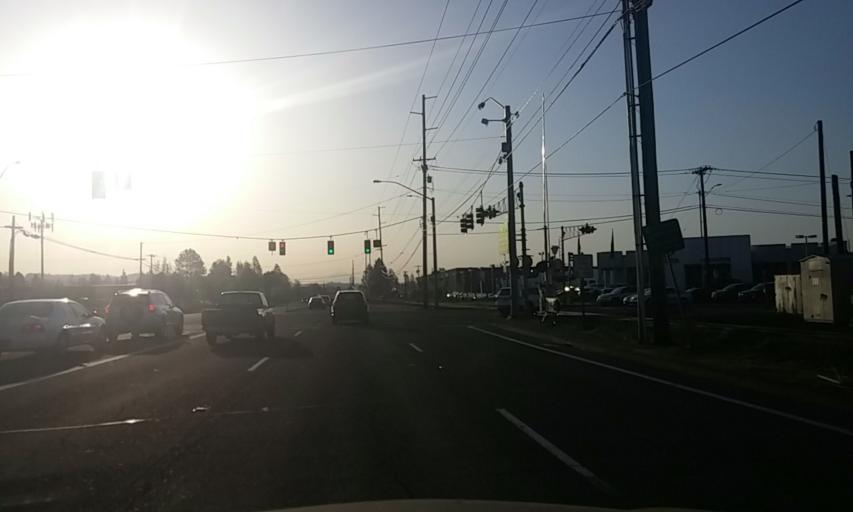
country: US
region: Oregon
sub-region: Washington County
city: Beaverton
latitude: 45.4896
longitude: -122.8267
